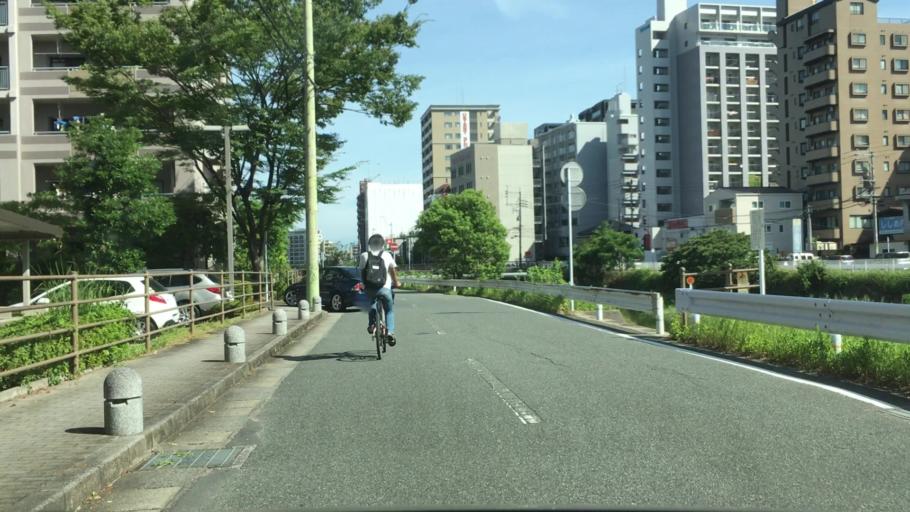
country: JP
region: Fukuoka
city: Fukuoka-shi
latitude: 33.5745
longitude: 130.3752
